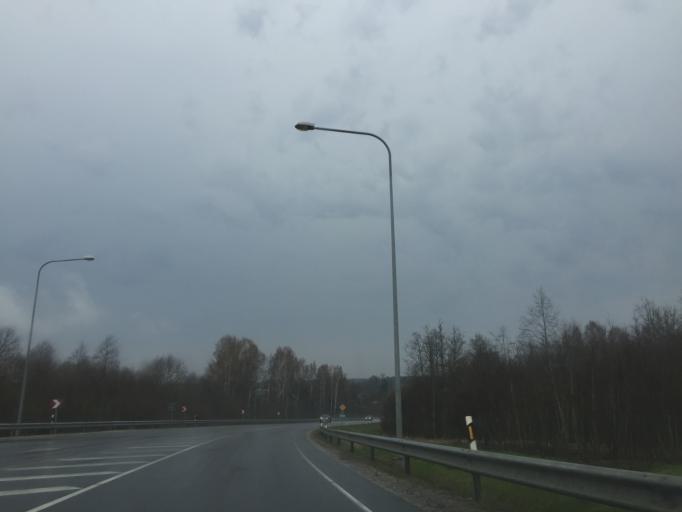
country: EE
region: Tartu
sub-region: UElenurme vald
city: Ulenurme
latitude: 58.2484
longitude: 26.6786
